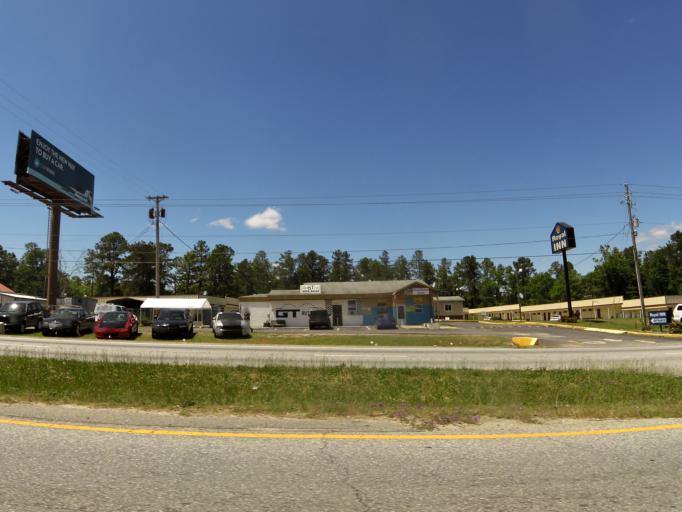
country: US
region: South Carolina
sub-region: Aiken County
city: Clearwater
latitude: 33.5009
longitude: -81.9072
